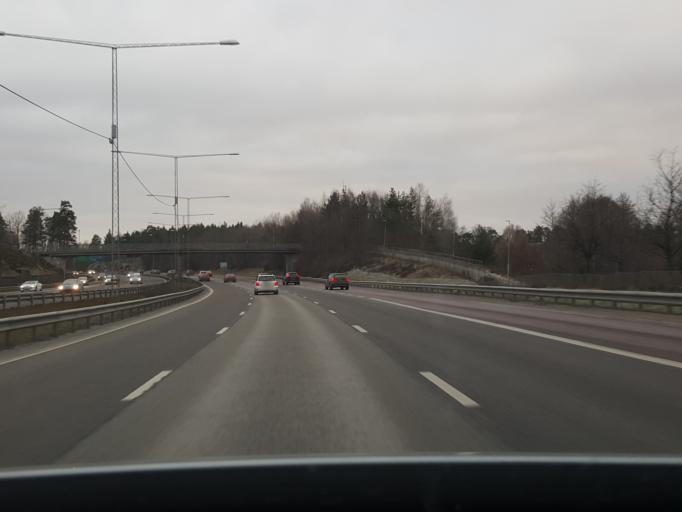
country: SE
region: Stockholm
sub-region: Botkyrka Kommun
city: Fittja
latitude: 59.2632
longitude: 17.8941
